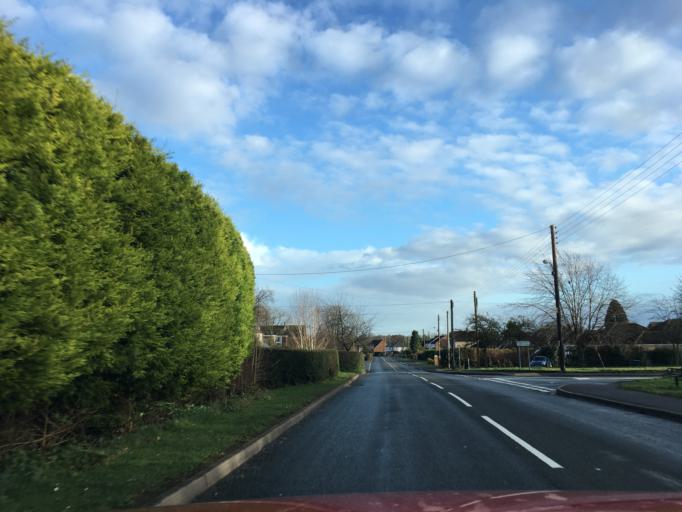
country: GB
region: England
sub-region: Warwickshire
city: Stratford-upon-Avon
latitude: 52.2224
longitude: -1.7677
